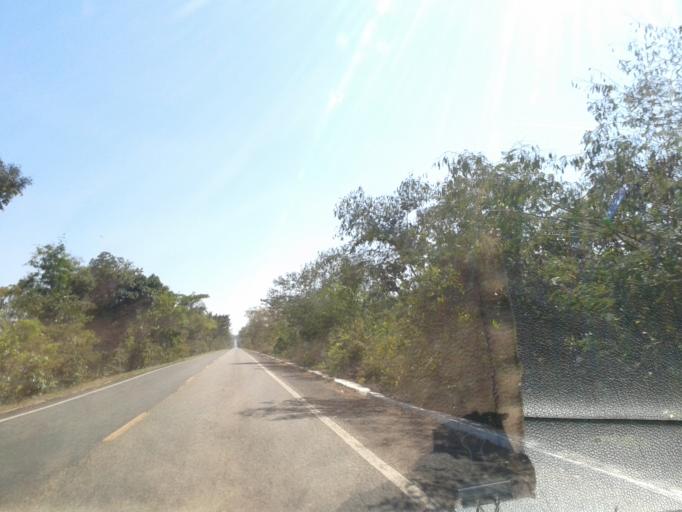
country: BR
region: Goias
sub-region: Crixas
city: Crixas
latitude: -13.9974
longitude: -50.3243
